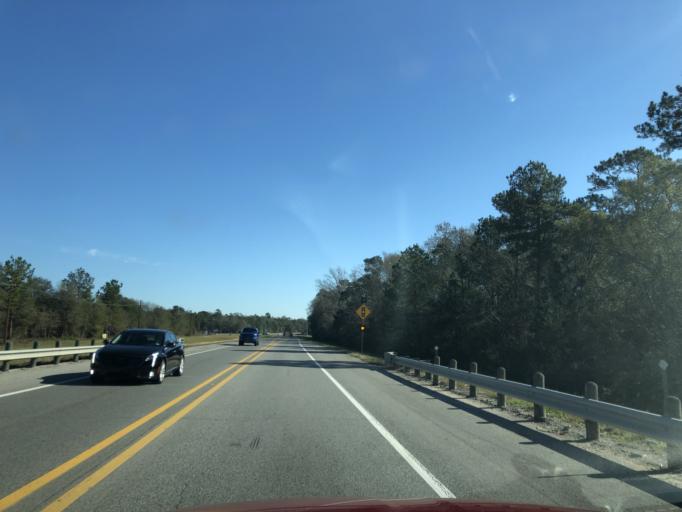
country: US
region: Texas
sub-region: Montgomery County
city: Porter Heights
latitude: 30.2141
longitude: -95.3085
